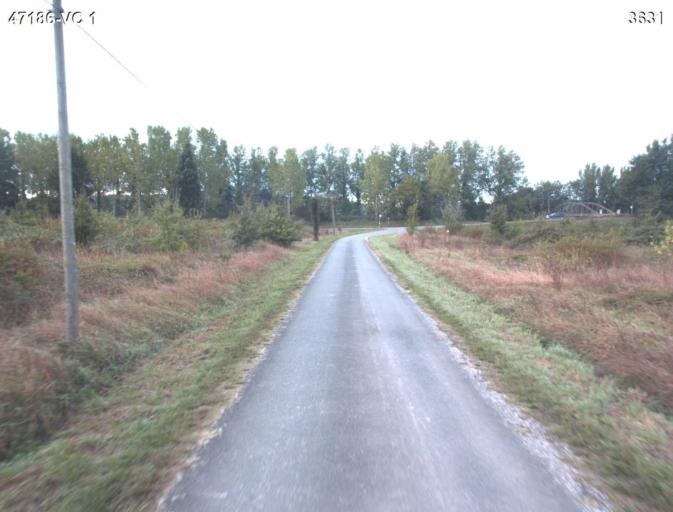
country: FR
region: Aquitaine
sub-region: Departement du Lot-et-Garonne
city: Port-Sainte-Marie
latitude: 44.2185
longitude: 0.4441
